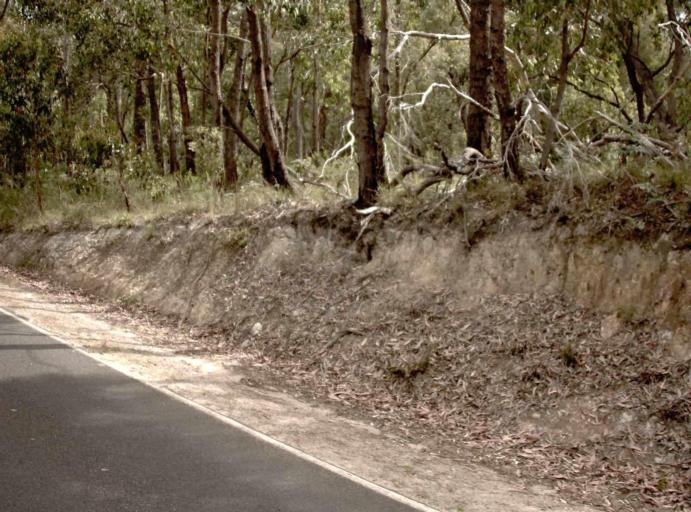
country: AU
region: Victoria
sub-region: Latrobe
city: Traralgon
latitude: -38.4186
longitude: 146.8165
